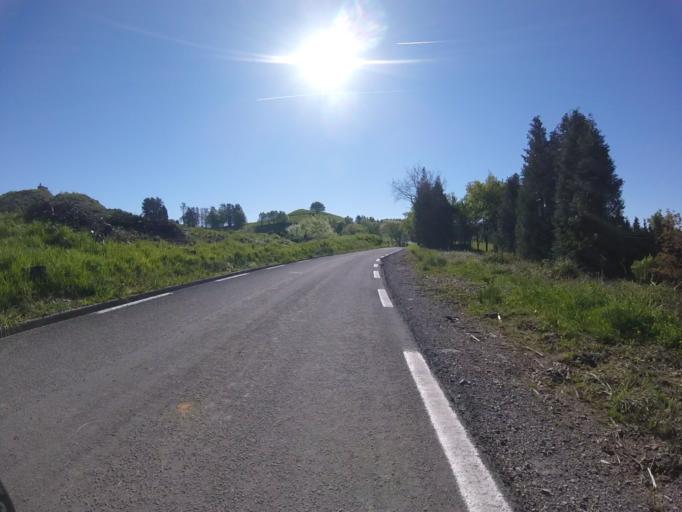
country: ES
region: Basque Country
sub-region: Provincia de Guipuzcoa
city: Aizarnazabal
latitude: 43.2177
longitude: -2.2140
